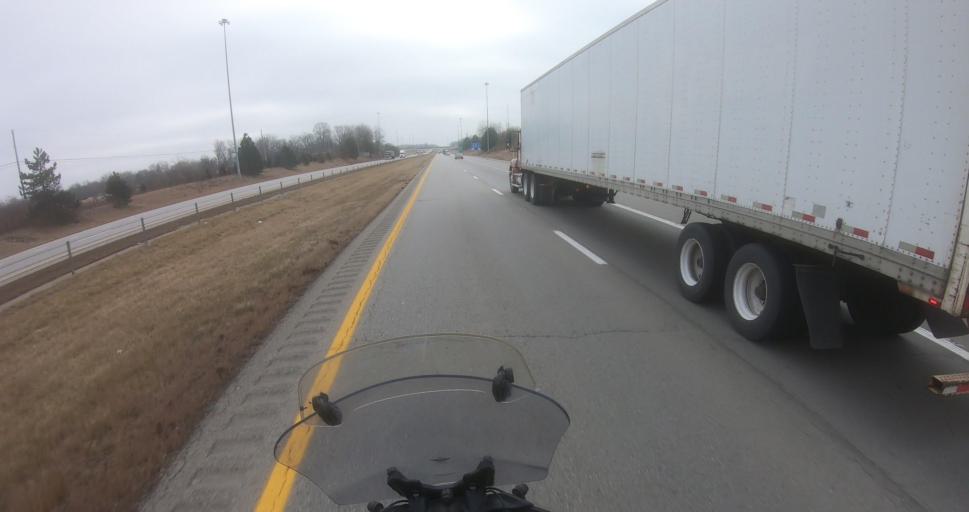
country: US
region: Ohio
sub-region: Miami County
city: Piqua
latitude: 40.1595
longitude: -84.2241
